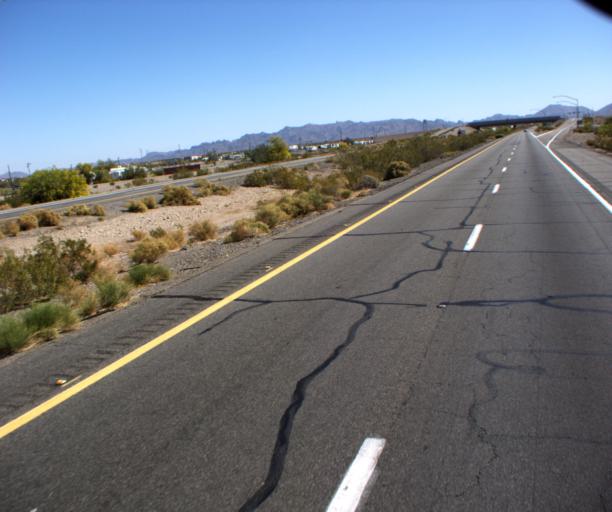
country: US
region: Arizona
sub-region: La Paz County
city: Quartzsite
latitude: 33.6644
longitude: -114.2069
